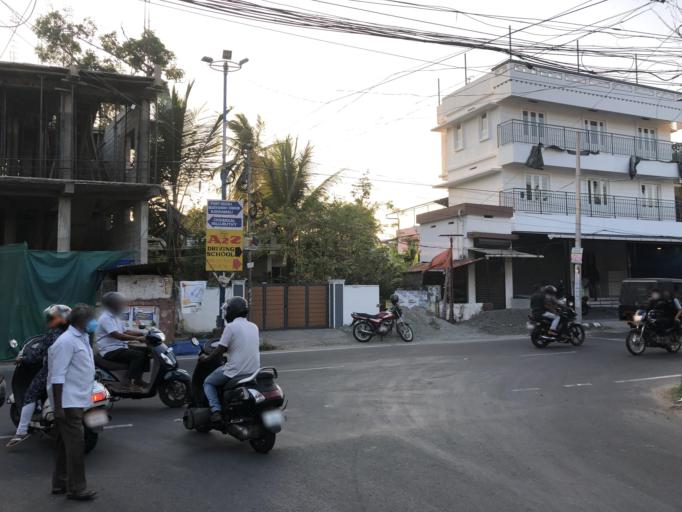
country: IN
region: Kerala
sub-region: Ernakulam
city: Cochin
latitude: 9.9313
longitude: 76.2627
